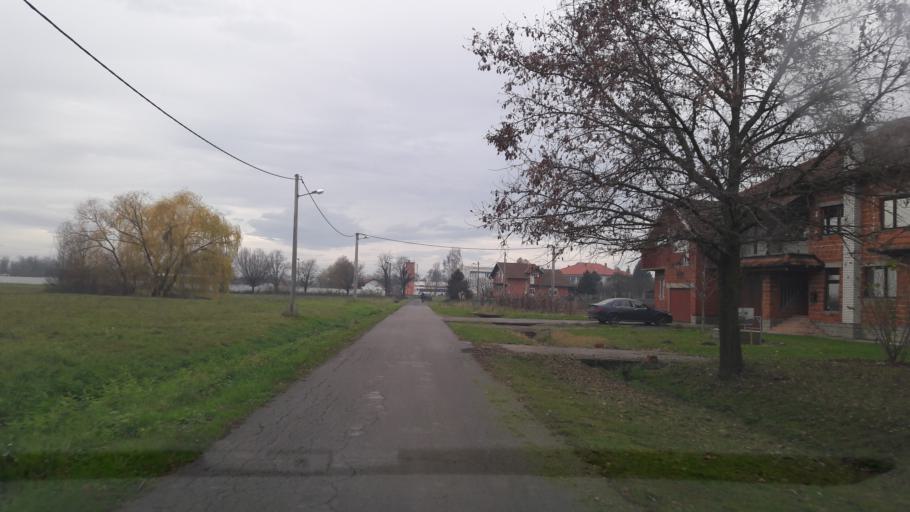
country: HR
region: Osjecko-Baranjska
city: Koska
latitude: 45.5427
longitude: 18.2884
